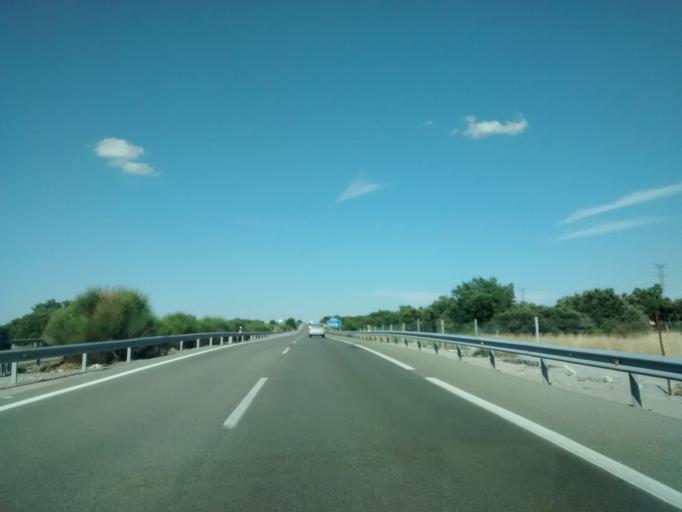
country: ES
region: Castille-La Mancha
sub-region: Provincia de Guadalajara
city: Torremocha del Campo
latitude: 41.0014
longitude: -2.5744
